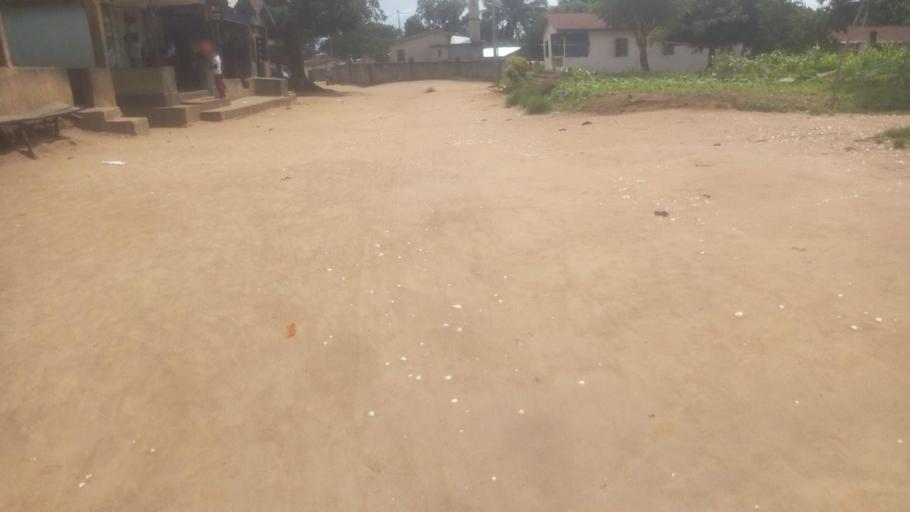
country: SL
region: Western Area
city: Freetown
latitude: 8.5241
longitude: -13.1492
